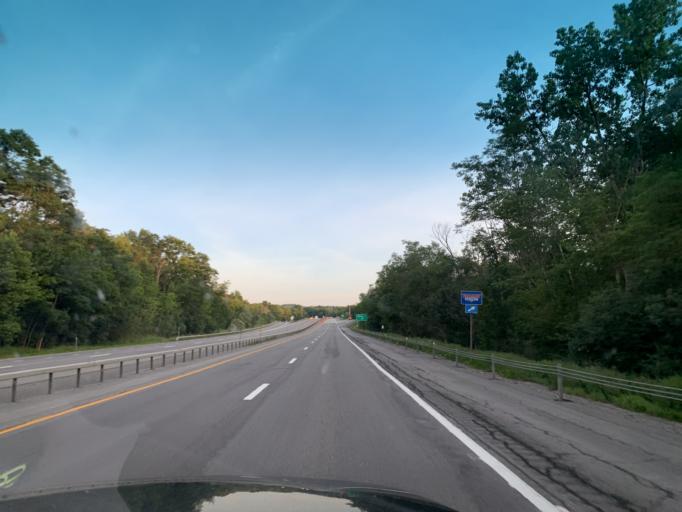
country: US
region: New York
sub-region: Oneida County
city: Chadwicks
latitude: 43.0106
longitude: -75.2547
